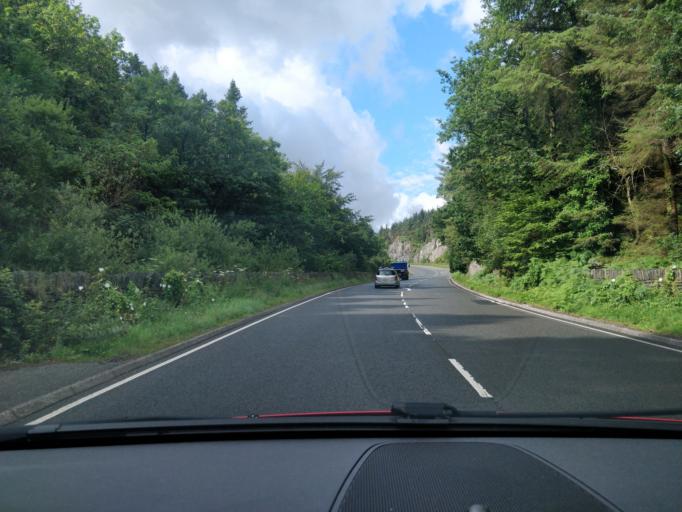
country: GB
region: Wales
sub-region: Gwynedd
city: Blaenau-Ffestiniog
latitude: 53.0418
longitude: -3.9197
